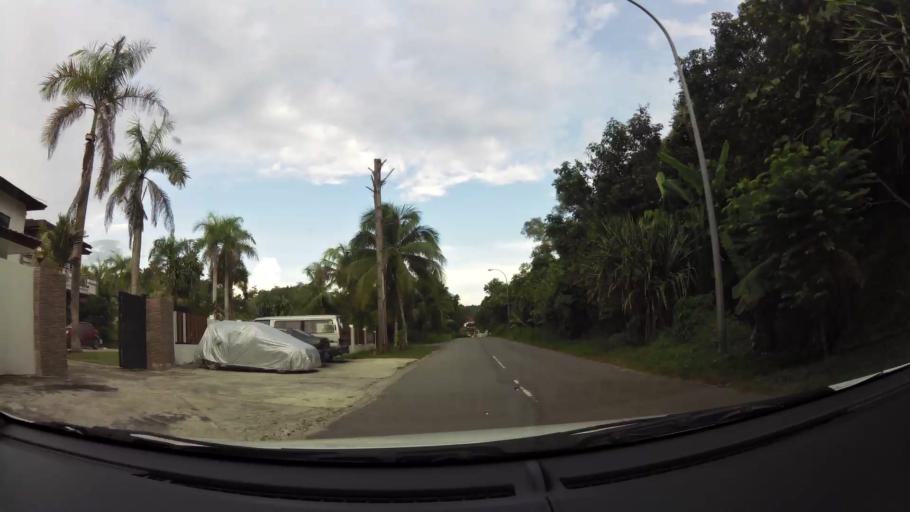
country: BN
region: Brunei and Muara
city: Bandar Seri Begawan
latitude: 4.9626
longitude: 114.9863
